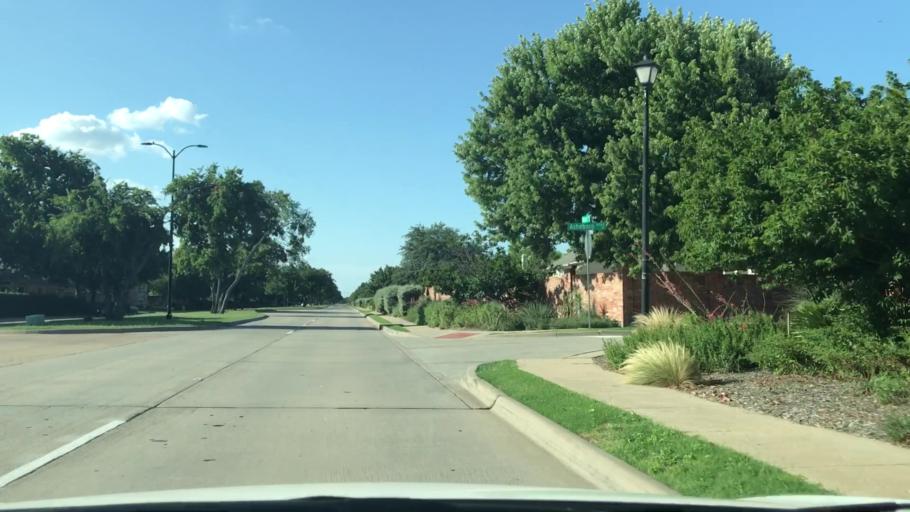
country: US
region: Texas
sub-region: Collin County
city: Frisco
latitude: 33.1181
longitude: -96.7880
